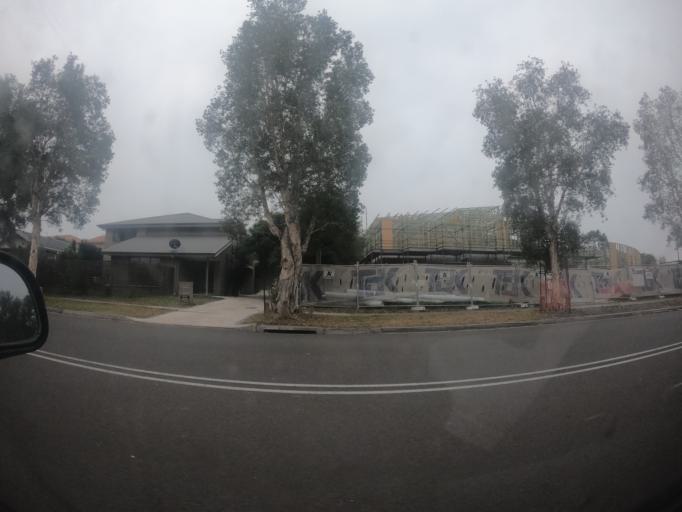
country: AU
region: New South Wales
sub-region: Shellharbour
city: Flinders
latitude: -34.5835
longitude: 150.8484
